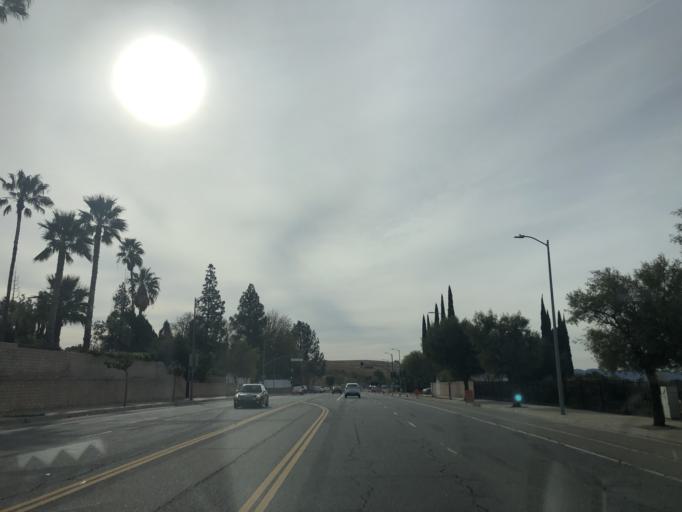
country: US
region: California
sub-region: Los Angeles County
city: Chatsworth
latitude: 34.2651
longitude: -118.5636
